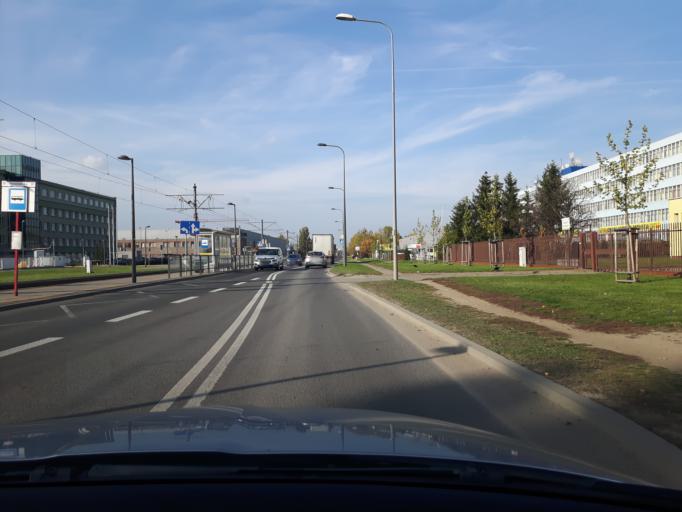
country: PL
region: Masovian Voivodeship
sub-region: Warszawa
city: Targowek
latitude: 52.3006
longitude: 21.0220
